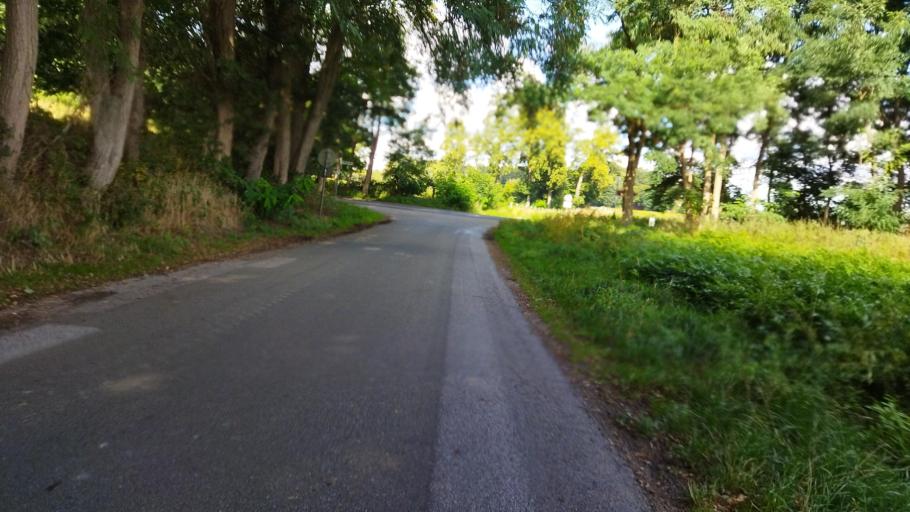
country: DE
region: Lower Saxony
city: Emsburen
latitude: 52.3925
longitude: 7.3246
